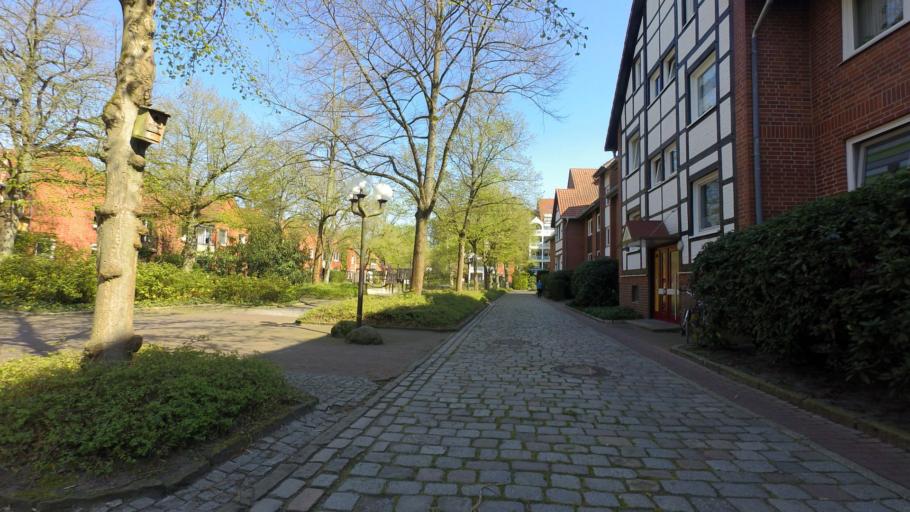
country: DE
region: Lower Saxony
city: Celle
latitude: 52.6214
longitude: 10.0930
